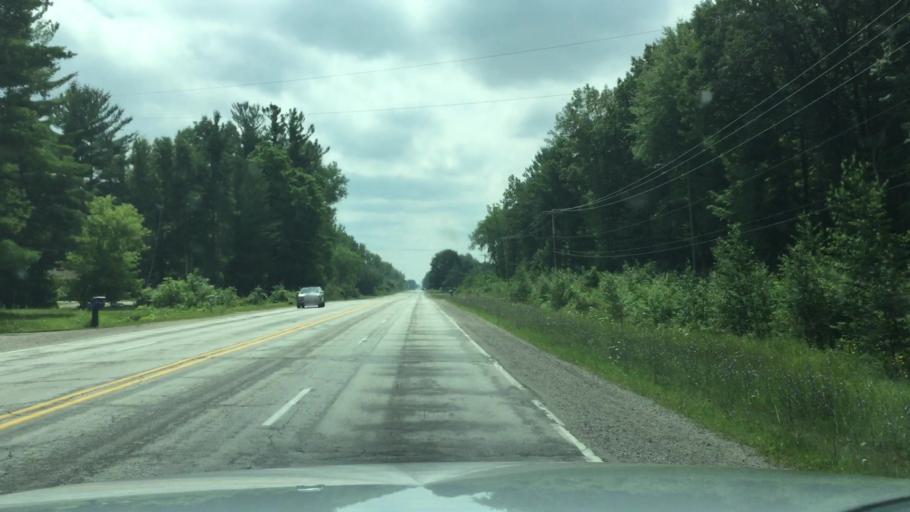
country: US
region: Michigan
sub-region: Saginaw County
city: Birch Run
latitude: 43.2864
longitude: -83.7968
